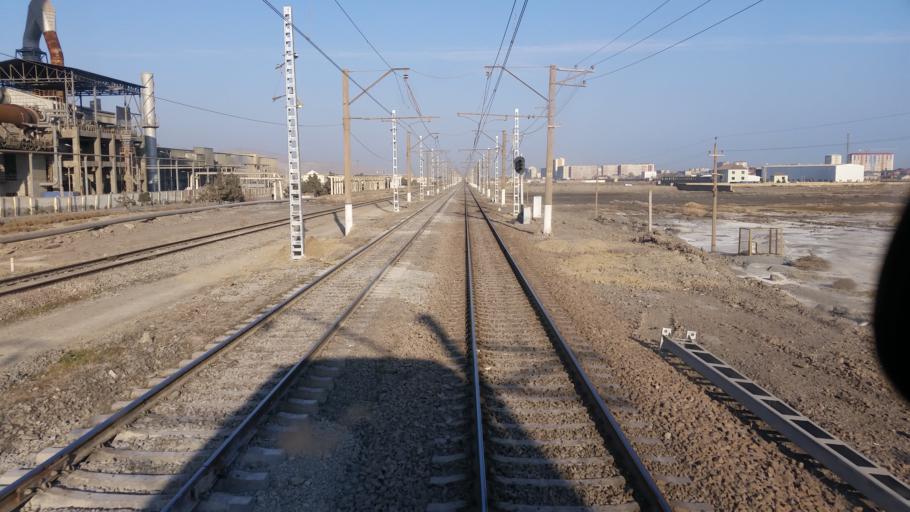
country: AZ
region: Baki
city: Korgoz
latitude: 40.2212
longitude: 49.5559
